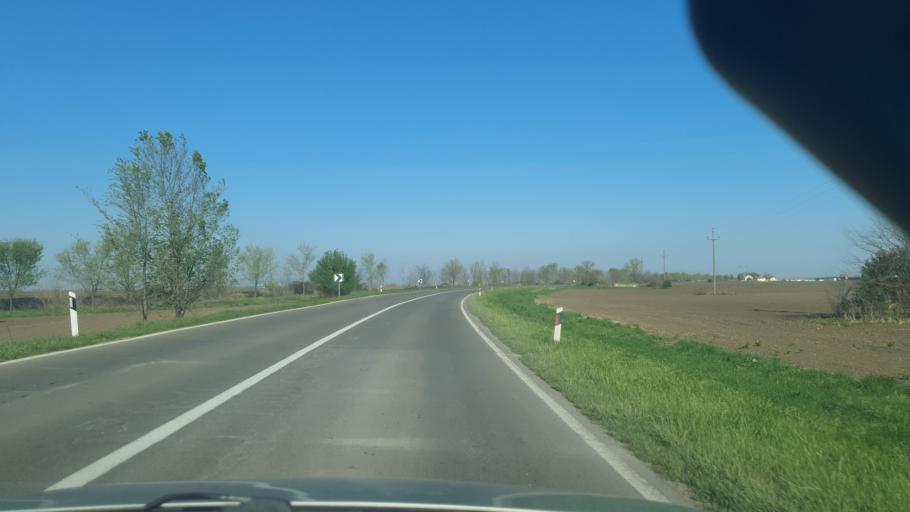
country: RS
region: Autonomna Pokrajina Vojvodina
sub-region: Zapadnobacki Okrug
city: Kula
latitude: 45.7213
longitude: 19.3695
